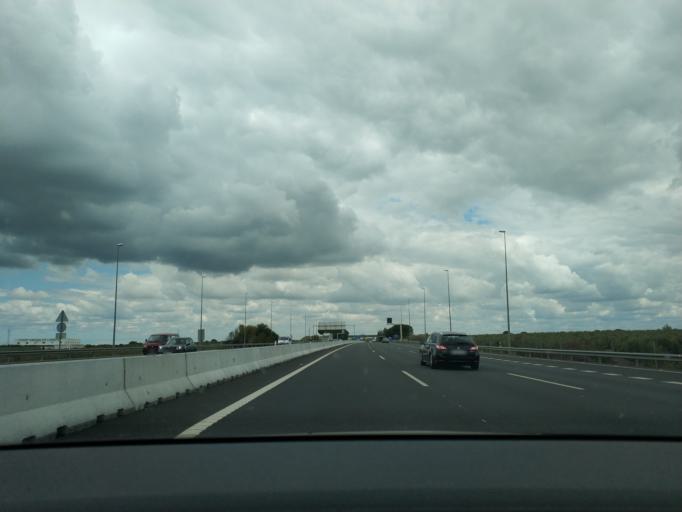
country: ES
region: Andalusia
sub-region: Provincia de Sevilla
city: Umbrete
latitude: 37.3572
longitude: -6.1752
